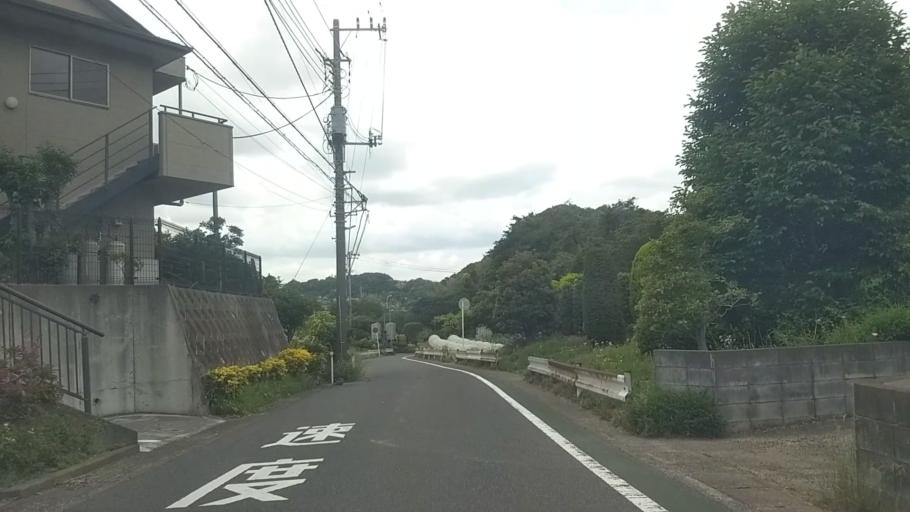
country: JP
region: Kanagawa
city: Fujisawa
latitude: 35.3566
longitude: 139.5101
